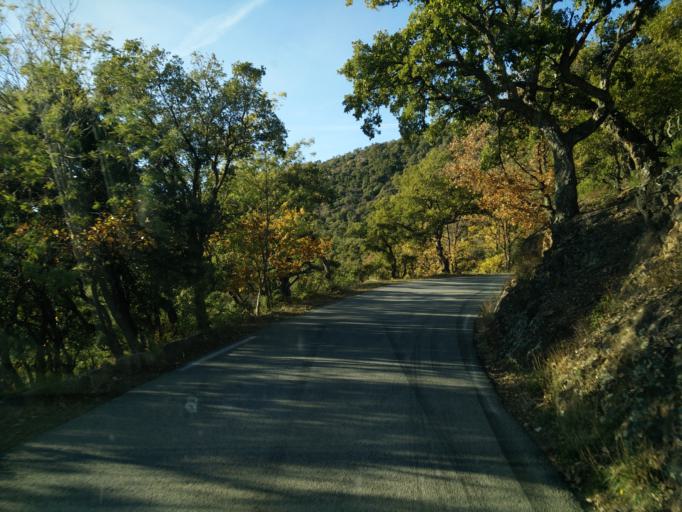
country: FR
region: Provence-Alpes-Cote d'Azur
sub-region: Departement du Var
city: Le Plan-de-la-Tour
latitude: 43.3370
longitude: 6.5189
